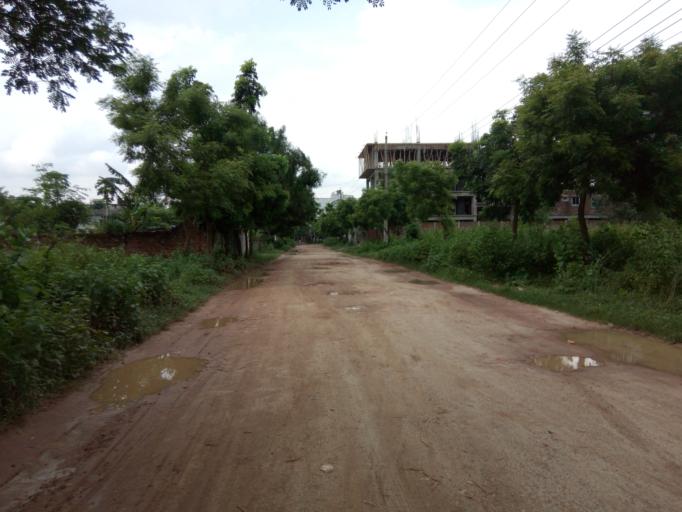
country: BD
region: Dhaka
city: Azimpur
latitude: 23.7522
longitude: 90.3435
